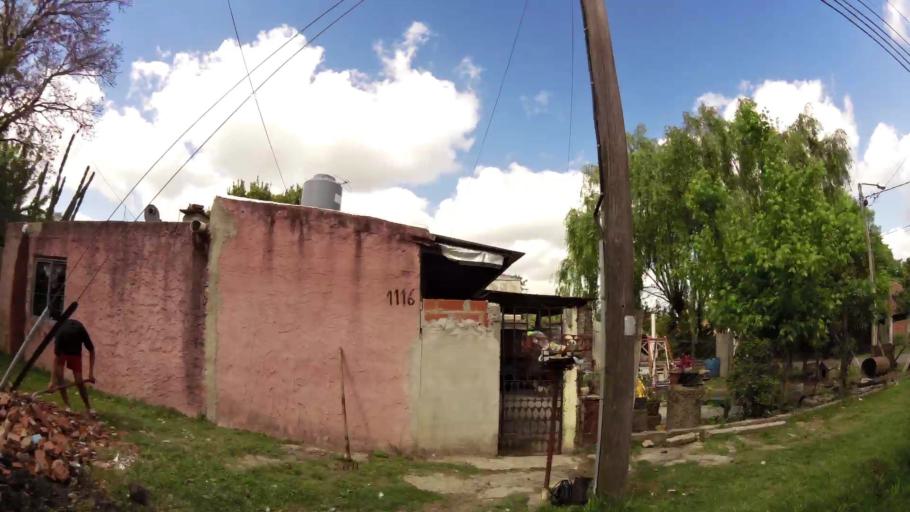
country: AR
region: Buenos Aires
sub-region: Partido de Quilmes
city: Quilmes
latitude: -34.8347
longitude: -58.1885
